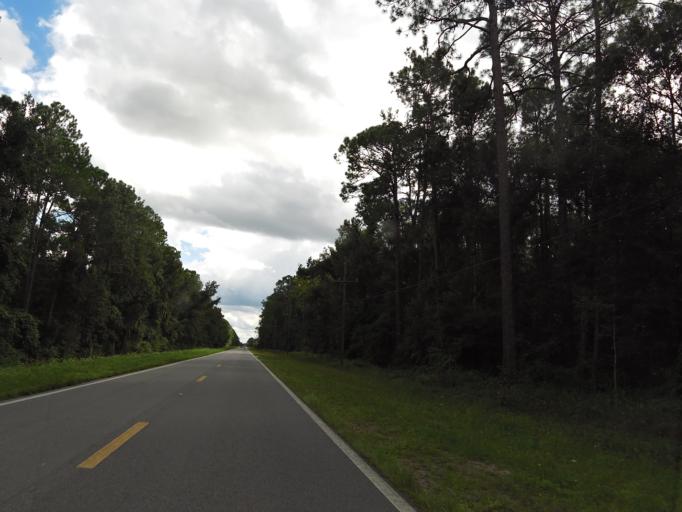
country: US
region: Florida
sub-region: Saint Johns County
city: Saint Augustine
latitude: 29.8746
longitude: -81.4944
